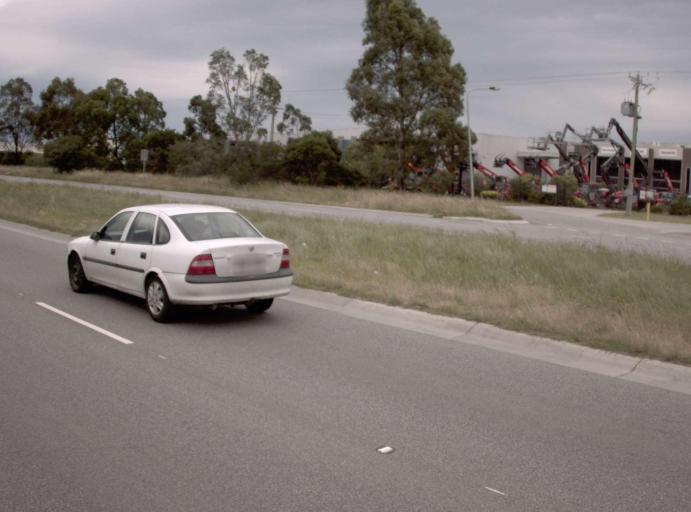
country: AU
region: Victoria
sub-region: Casey
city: Hampton Park
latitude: -38.0305
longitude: 145.2443
